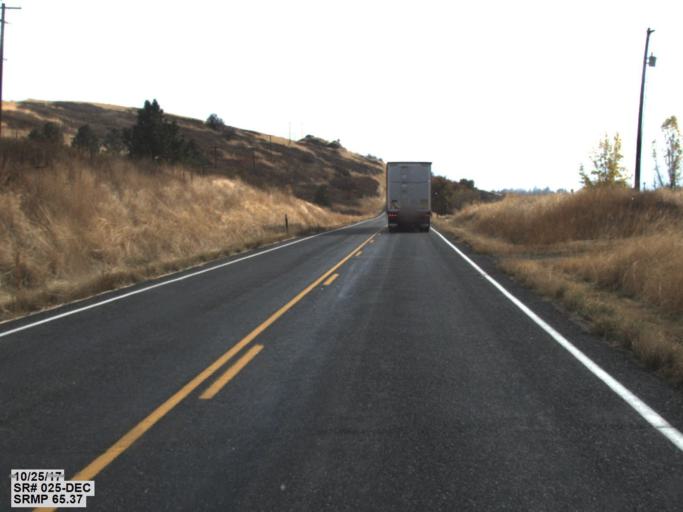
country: US
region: Washington
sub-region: Stevens County
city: Kettle Falls
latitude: 48.4151
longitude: -118.1718
